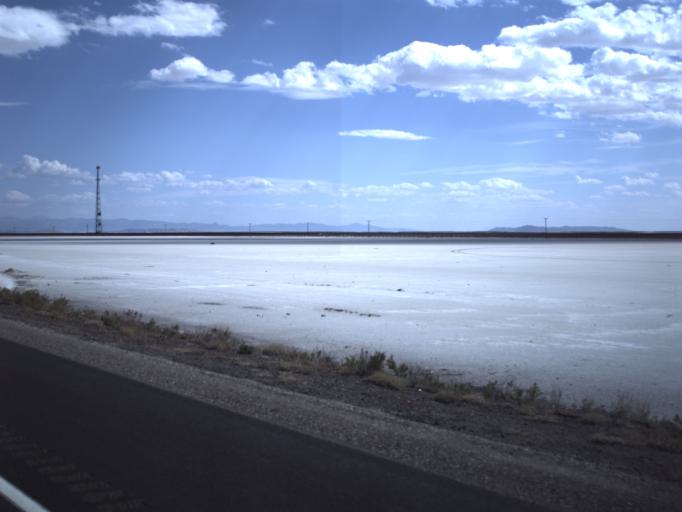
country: US
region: Utah
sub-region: Tooele County
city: Wendover
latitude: 40.7325
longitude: -113.5719
